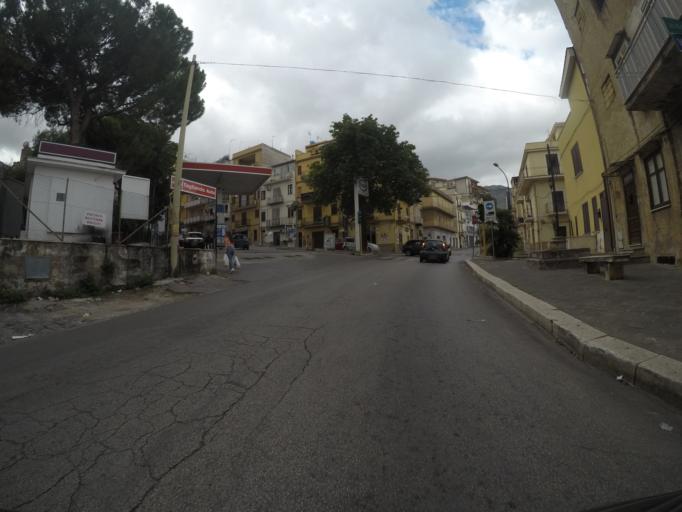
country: IT
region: Sicily
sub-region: Palermo
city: Carini
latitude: 38.1340
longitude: 13.1864
